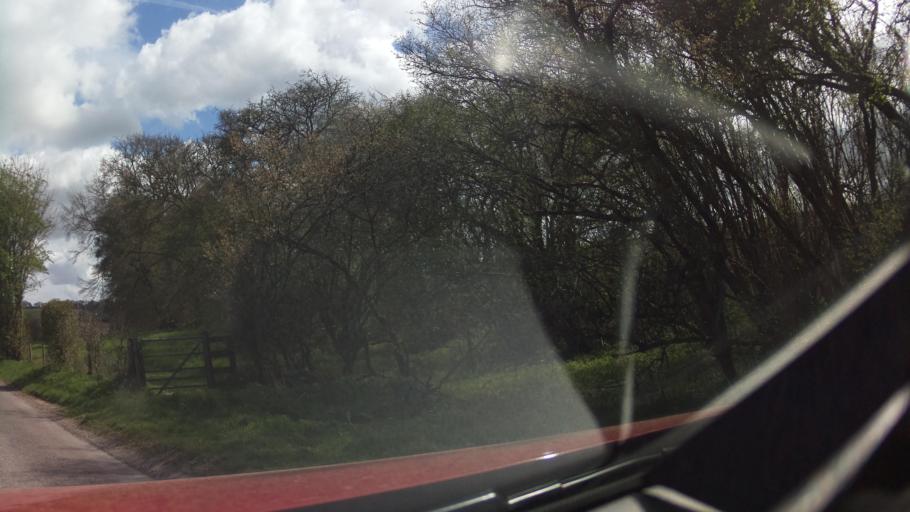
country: GB
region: England
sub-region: West Berkshire
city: Kintbury
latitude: 51.3257
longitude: -1.4671
